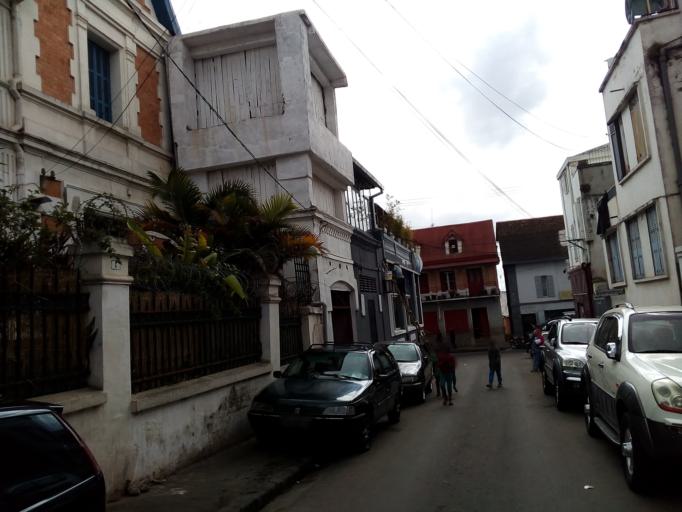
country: MG
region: Analamanga
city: Antananarivo
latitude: -18.9111
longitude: 47.5210
